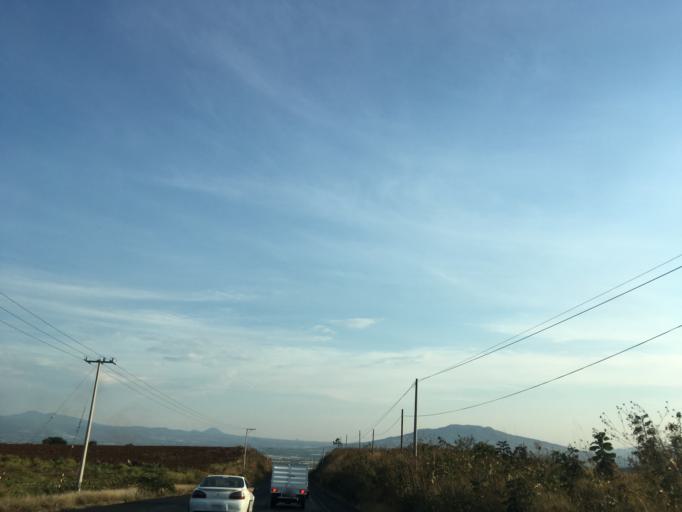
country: MX
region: Michoacan
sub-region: Los Reyes
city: La Higuerita (Colonia San Rafael)
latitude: 19.6662
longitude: -102.4925
